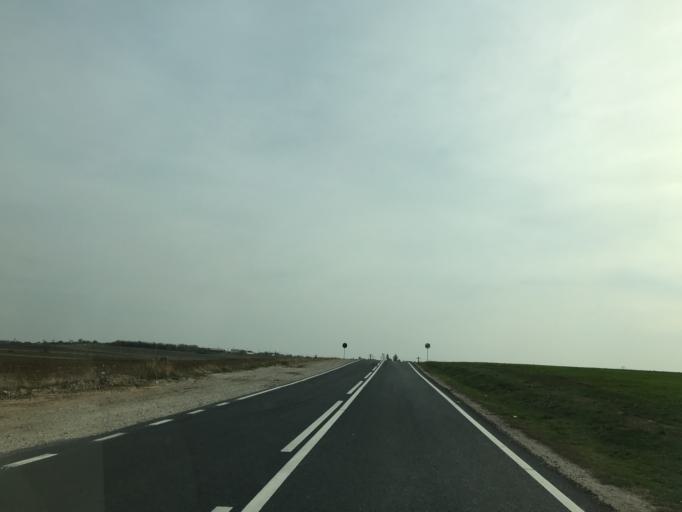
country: RO
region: Olt
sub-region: Comuna Brancoveni
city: Brancoveni
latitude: 44.3268
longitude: 24.2973
